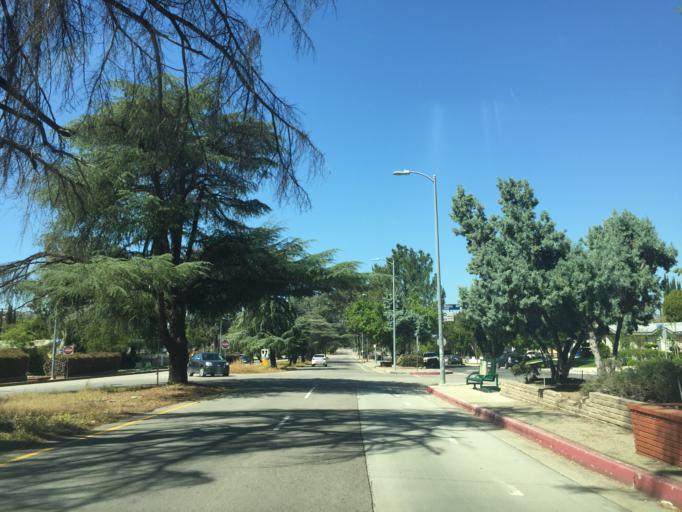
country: US
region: California
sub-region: Los Angeles County
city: Calabasas
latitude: 34.1513
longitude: -118.6258
